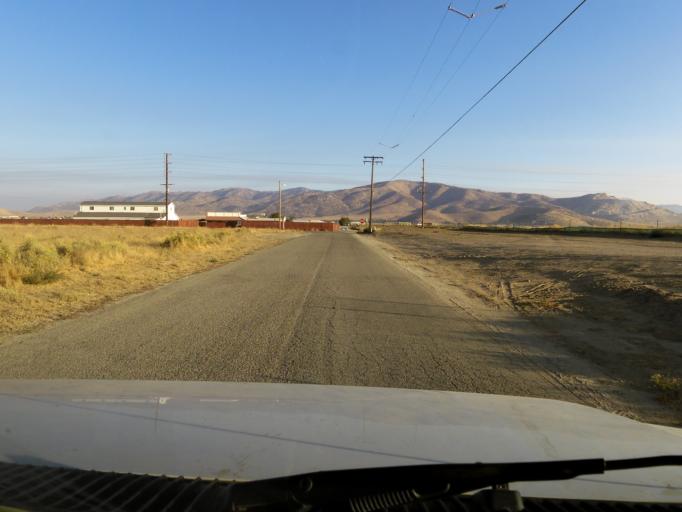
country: US
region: California
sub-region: Kern County
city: Tehachapi
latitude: 35.1089
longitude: -118.4236
